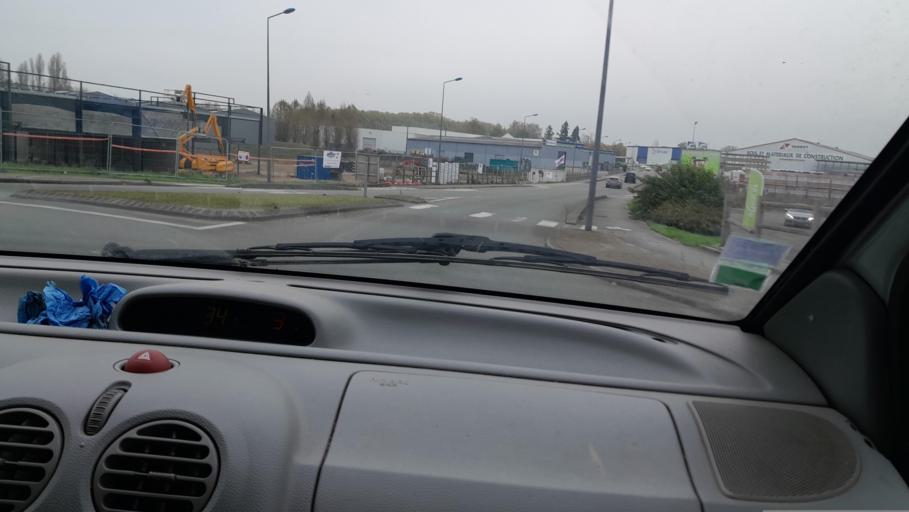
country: FR
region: Pays de la Loire
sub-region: Departement de la Mayenne
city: Saint-Berthevin
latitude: 48.0660
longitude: -0.8120
